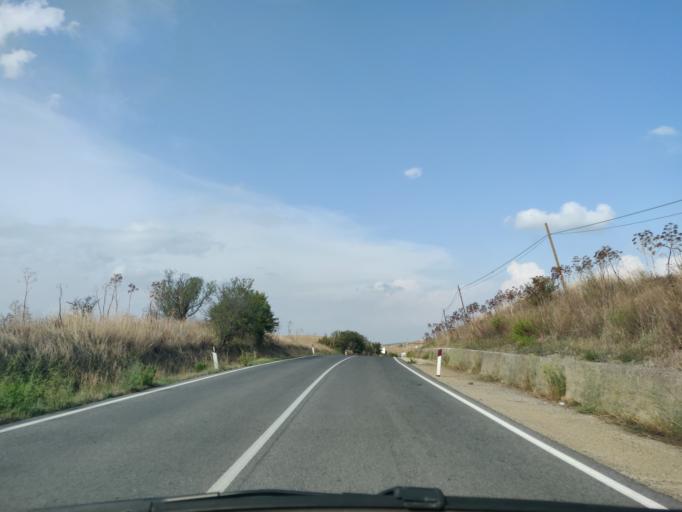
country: IT
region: Latium
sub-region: Provincia di Viterbo
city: Tarquinia
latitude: 42.2498
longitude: 11.8107
